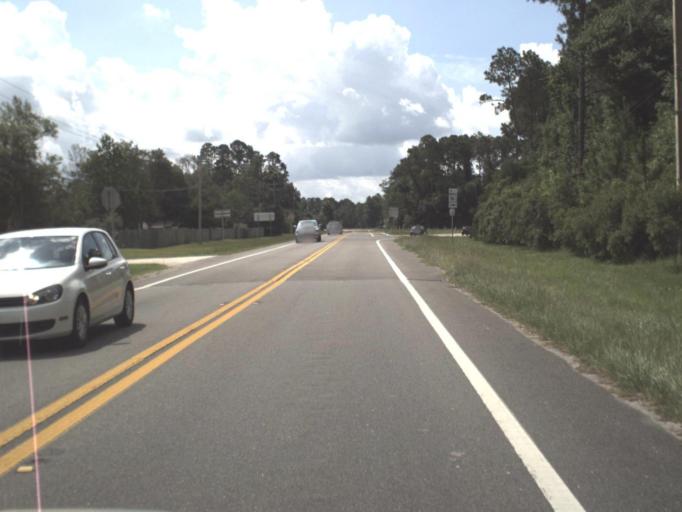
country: US
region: Florida
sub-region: Clay County
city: Green Cove Springs
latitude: 29.9994
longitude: -81.6012
